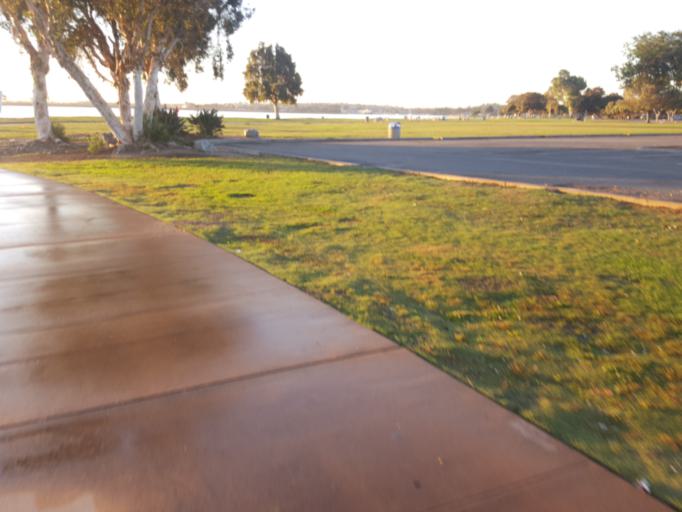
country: US
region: California
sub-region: San Diego County
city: La Jolla
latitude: 32.7864
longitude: -117.2324
